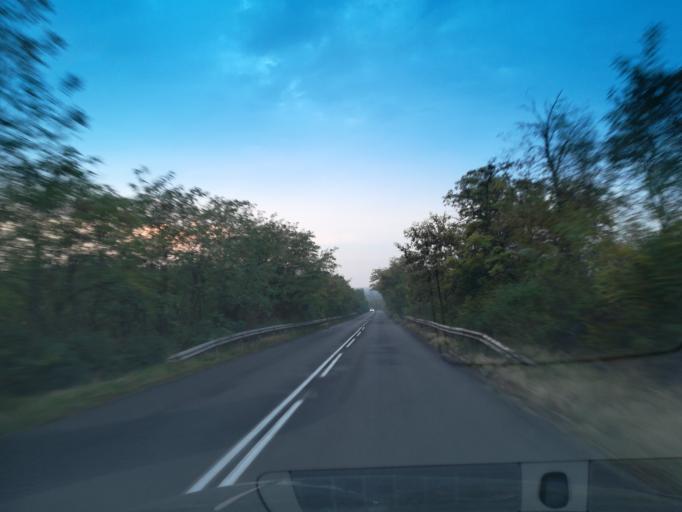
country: BG
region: Stara Zagora
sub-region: Obshtina Chirpan
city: Chirpan
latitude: 42.1797
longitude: 25.2268
